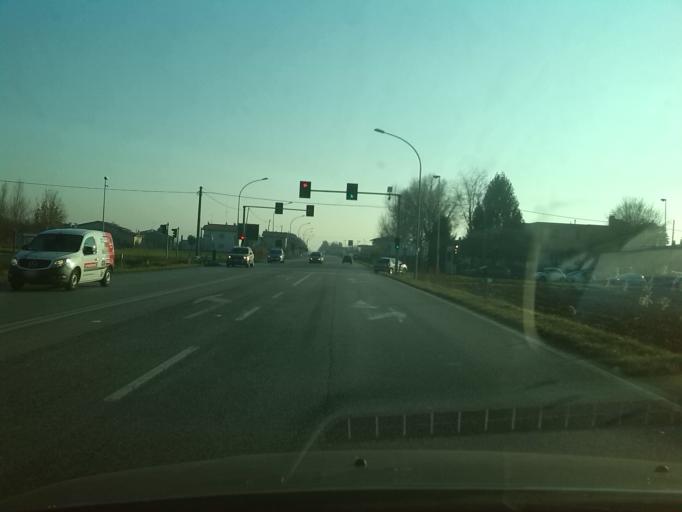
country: IT
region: Friuli Venezia Giulia
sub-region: Provincia di Udine
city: Latisana
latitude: 45.7738
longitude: 13.0226
